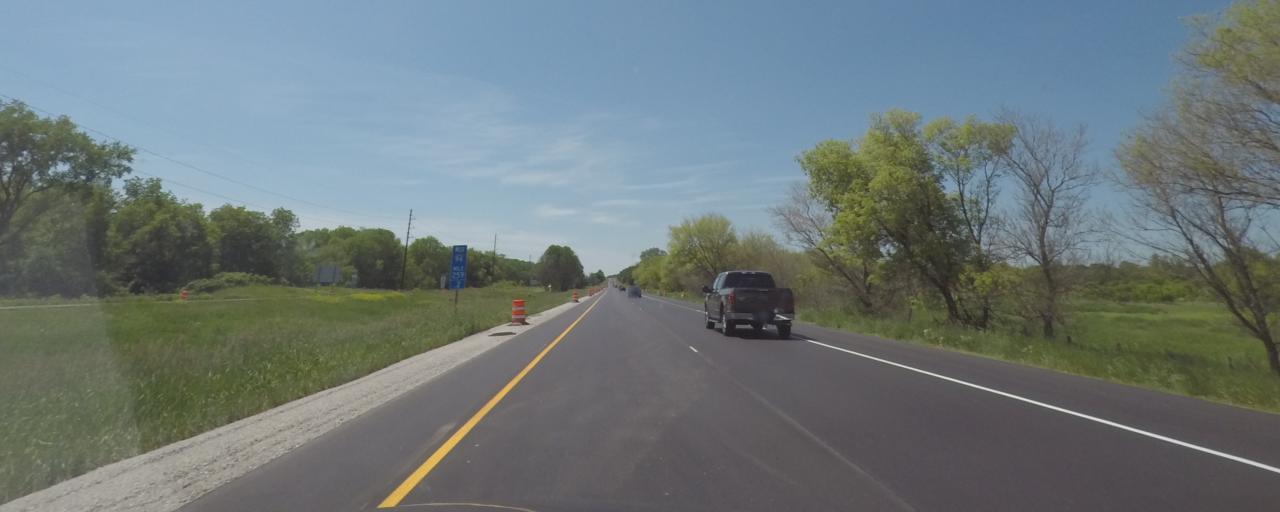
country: US
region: Wisconsin
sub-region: Jefferson County
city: Lake Mills
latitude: 43.0957
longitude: -88.9156
